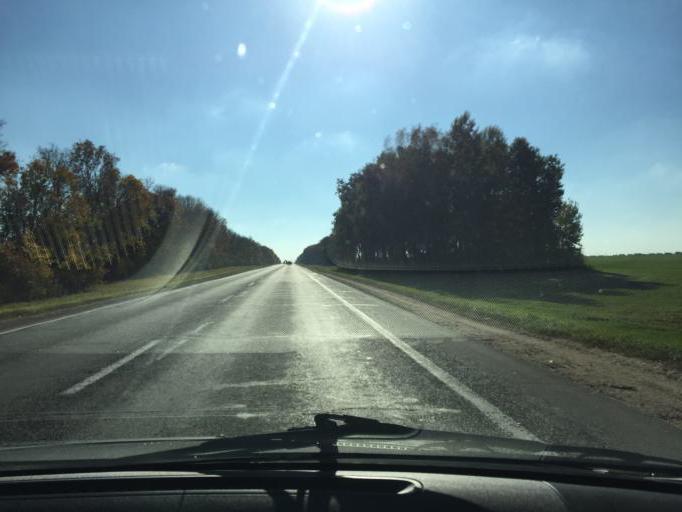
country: BY
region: Minsk
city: Slutsk
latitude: 52.9726
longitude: 27.5014
